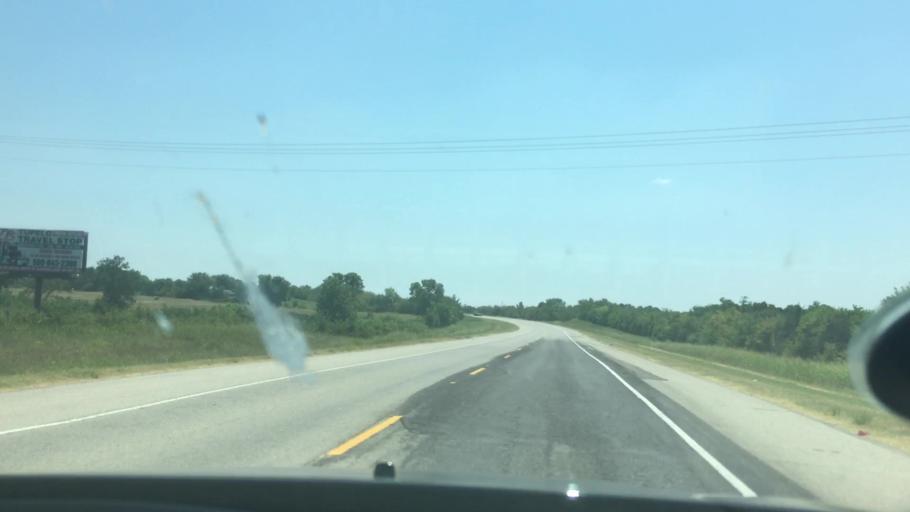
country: US
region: Oklahoma
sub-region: Pontotoc County
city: Ada
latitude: 34.6509
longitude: -96.5539
